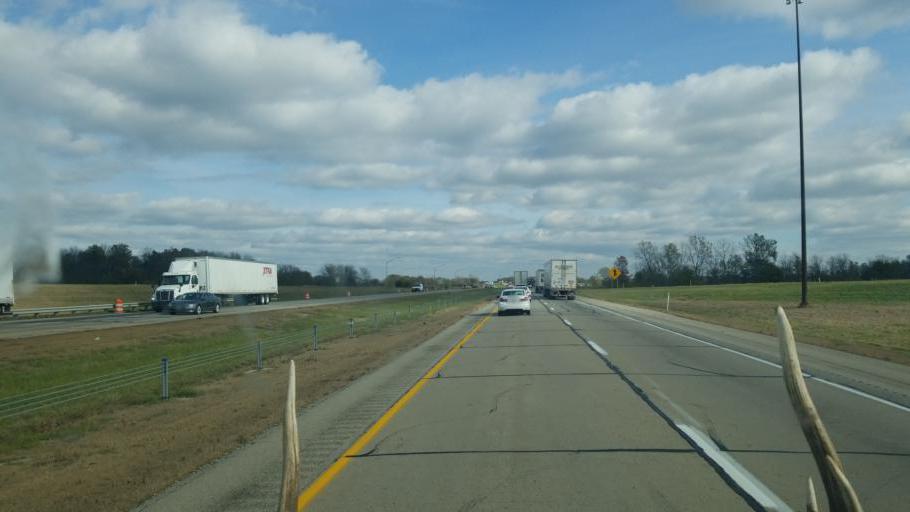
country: US
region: Indiana
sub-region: Wayne County
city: Cambridge City
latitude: 39.8520
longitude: -85.2623
